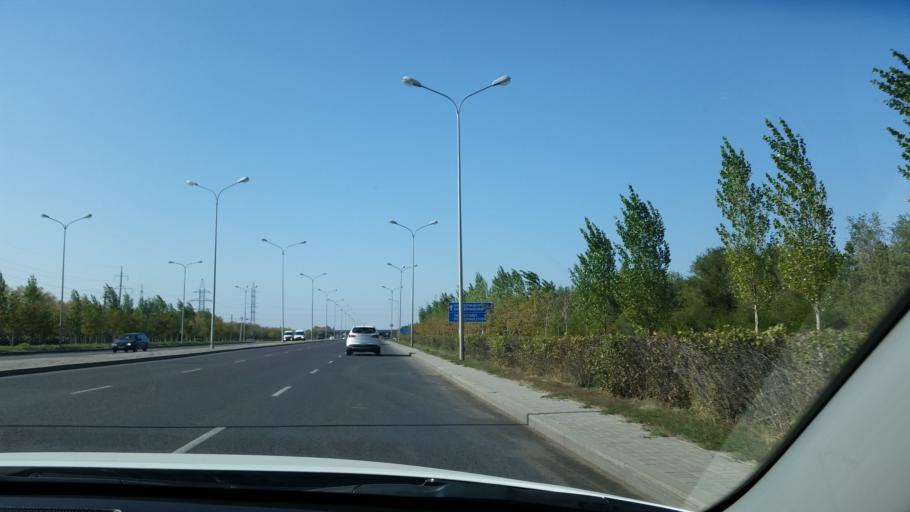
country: KZ
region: Astana Qalasy
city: Astana
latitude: 51.1970
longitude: 71.3150
